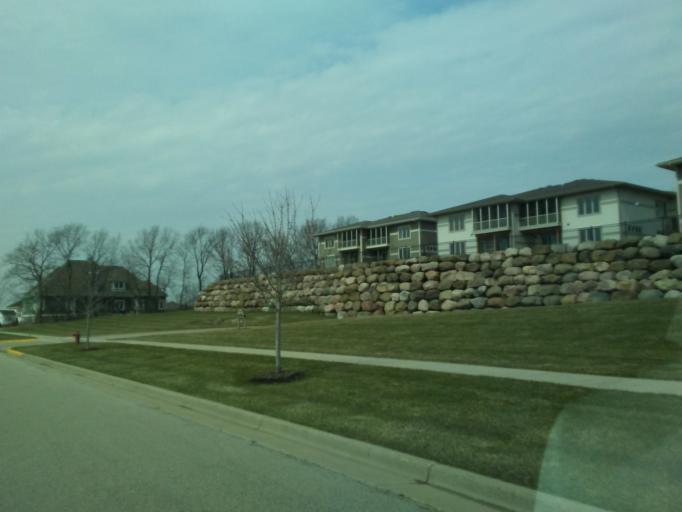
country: US
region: Wisconsin
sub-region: Dane County
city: Waunakee
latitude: 43.1723
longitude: -89.4458
